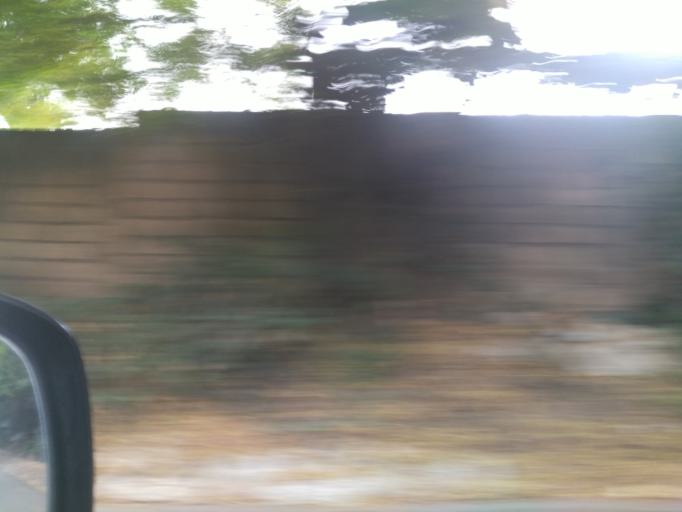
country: GH
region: Greater Accra
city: Accra
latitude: 5.5936
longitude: -0.1824
